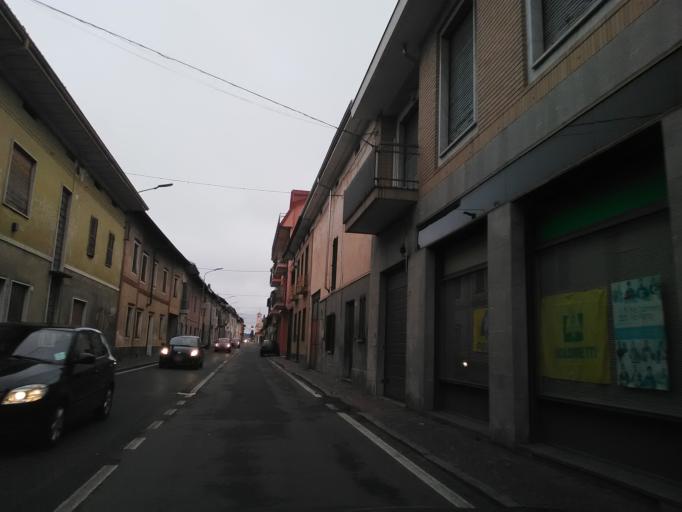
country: IT
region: Piedmont
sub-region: Provincia di Vercelli
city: Cigliano
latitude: 45.3093
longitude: 8.0183
